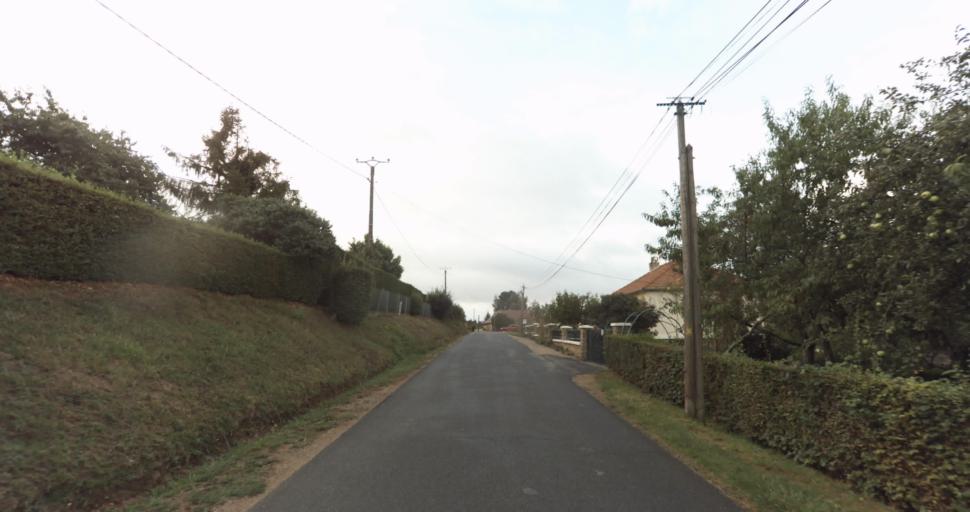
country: FR
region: Lower Normandy
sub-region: Departement de l'Orne
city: Vimoutiers
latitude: 48.9159
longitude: 0.2097
